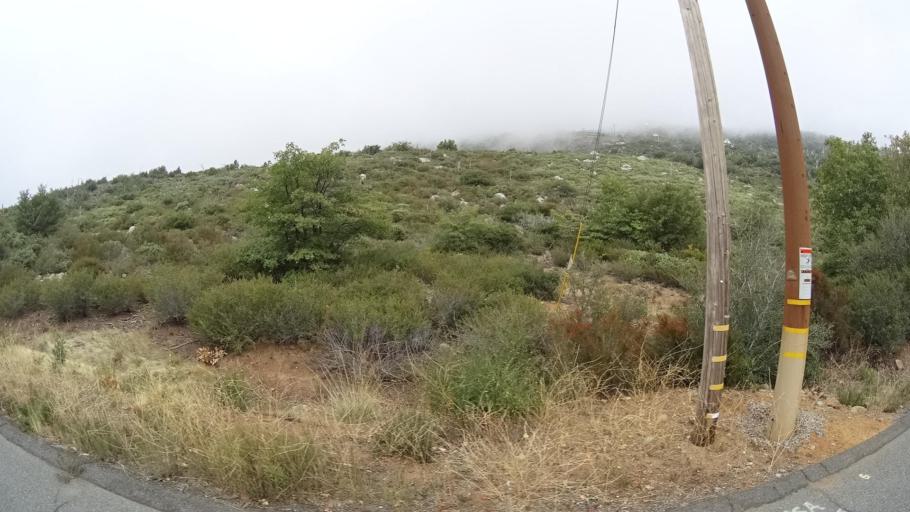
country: US
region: California
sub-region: San Diego County
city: Julian
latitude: 32.9967
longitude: -116.5922
